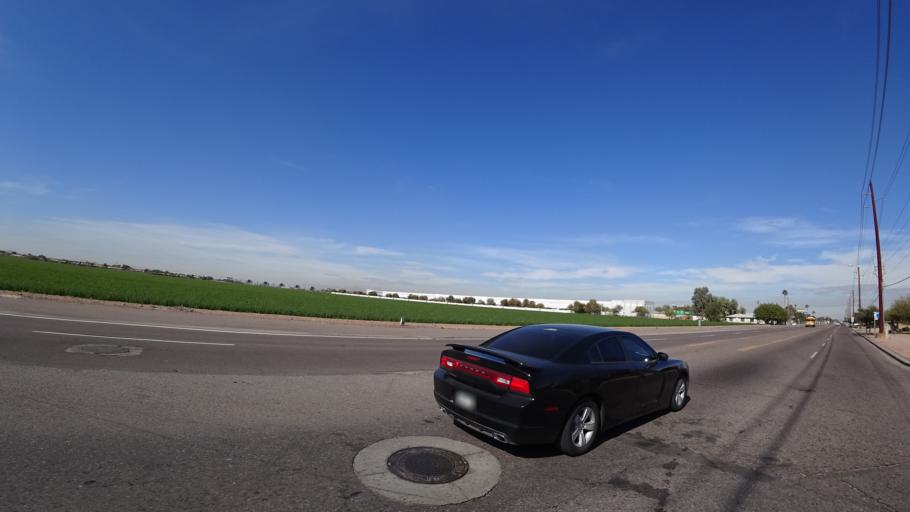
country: US
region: Arizona
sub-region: Maricopa County
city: Tolleson
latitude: 33.4299
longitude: -112.2038
